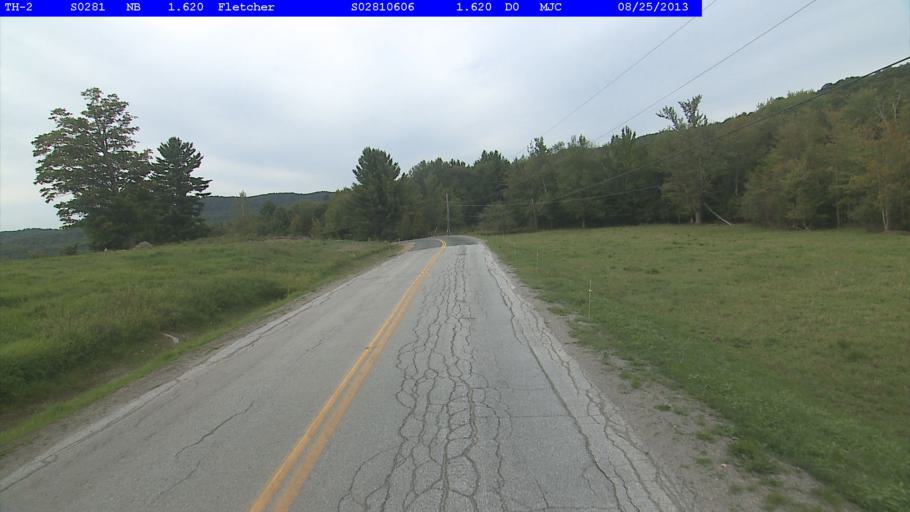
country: US
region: Vermont
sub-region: Chittenden County
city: Milton
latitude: 44.6985
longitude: -72.9353
